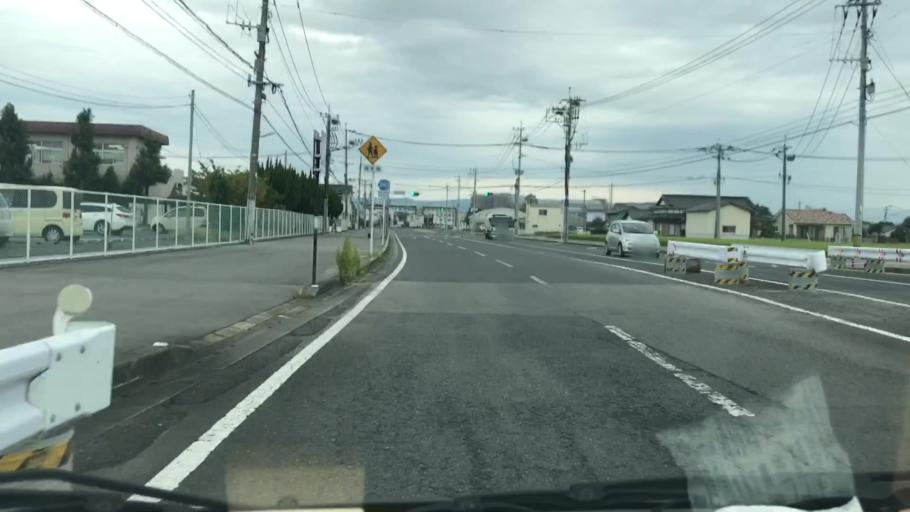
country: JP
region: Saga Prefecture
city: Saga-shi
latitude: 33.2315
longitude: 130.2938
